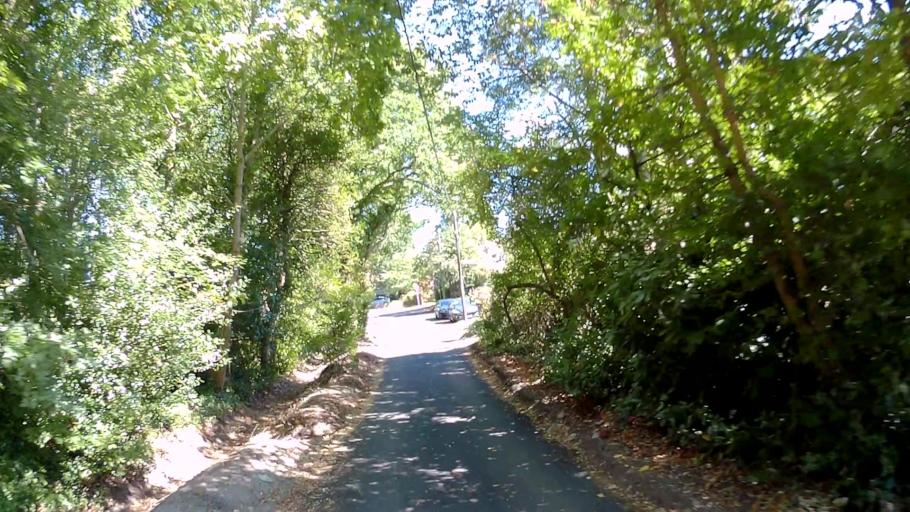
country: GB
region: England
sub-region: Bracknell Forest
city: Crowthorne
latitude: 51.3800
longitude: -0.7970
